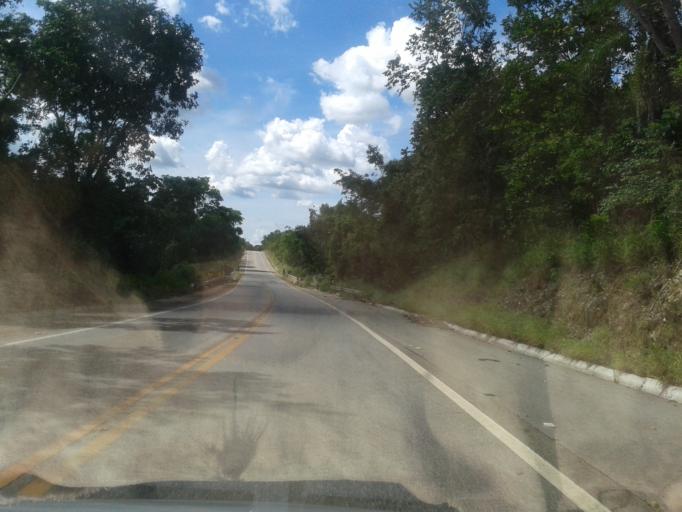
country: BR
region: Goias
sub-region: Itapuranga
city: Itapuranga
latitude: -15.5572
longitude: -50.2835
